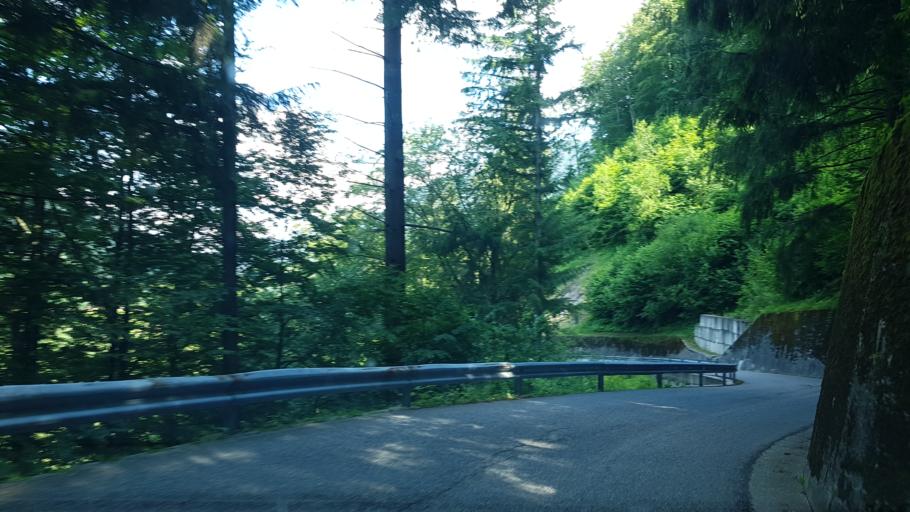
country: IT
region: Friuli Venezia Giulia
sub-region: Provincia di Udine
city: Pontebba
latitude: 46.5127
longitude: 13.2932
